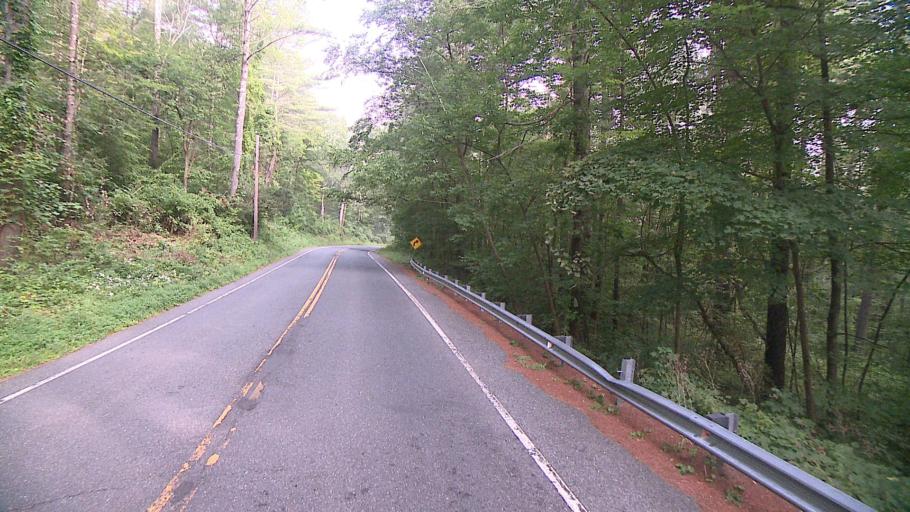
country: US
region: Connecticut
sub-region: Litchfield County
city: Canaan
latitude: 41.9157
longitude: -73.3658
